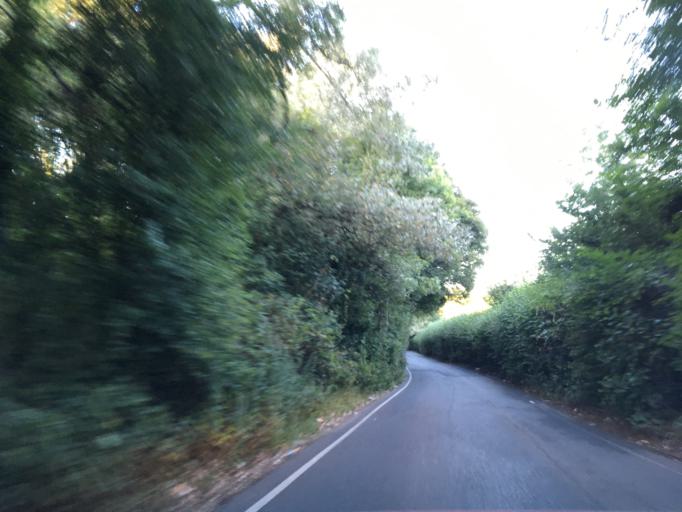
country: GB
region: England
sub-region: Bath and North East Somerset
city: Whitchurch
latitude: 51.4195
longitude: -2.5328
